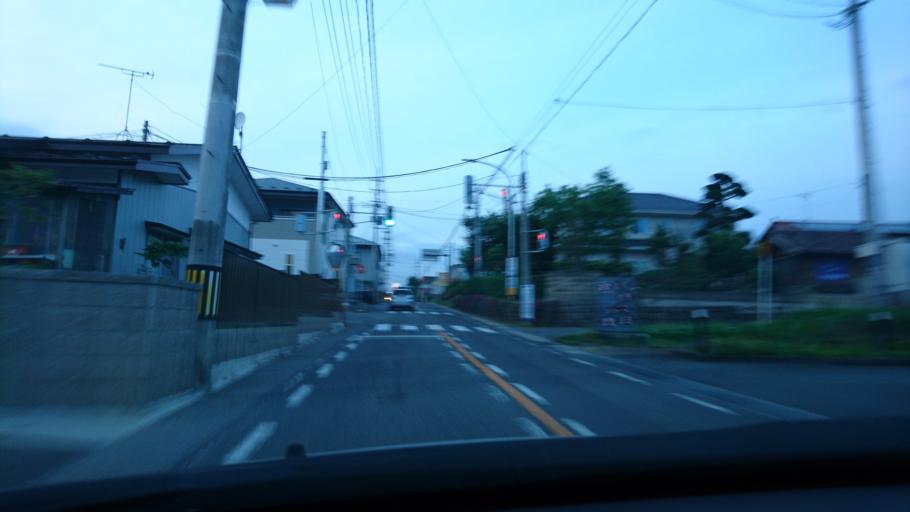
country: JP
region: Iwate
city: Ichinoseki
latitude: 38.8142
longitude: 140.9853
